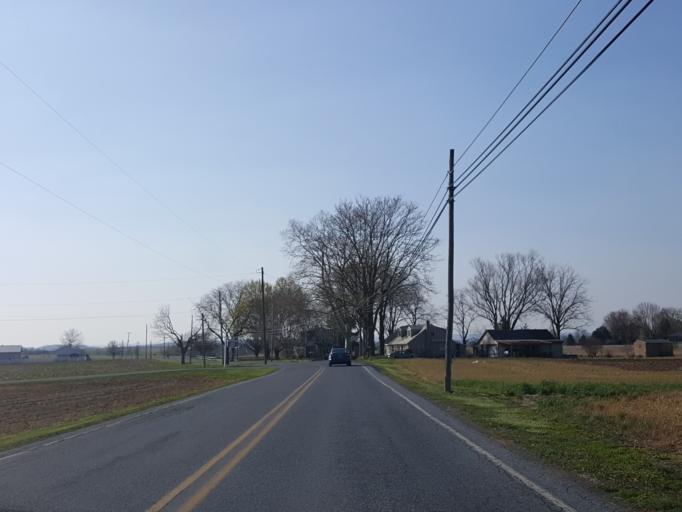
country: US
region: Pennsylvania
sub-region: Lebanon County
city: Annville
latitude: 40.3094
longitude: -76.5190
